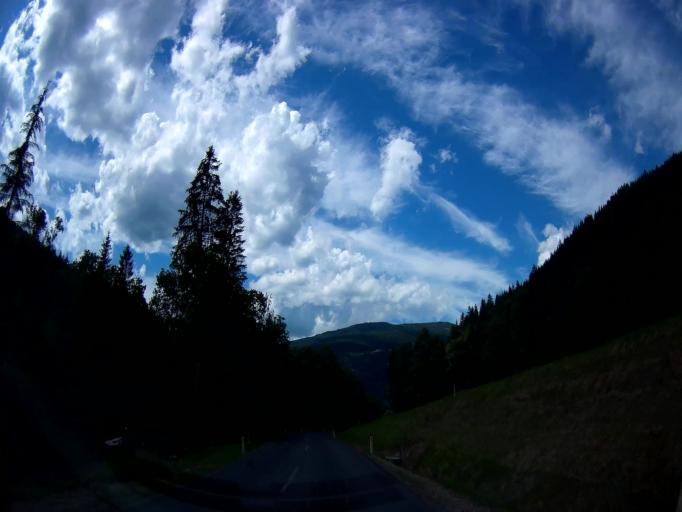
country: AT
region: Styria
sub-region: Politischer Bezirk Murau
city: Stadl an der Mur
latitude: 47.0703
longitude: 13.9852
